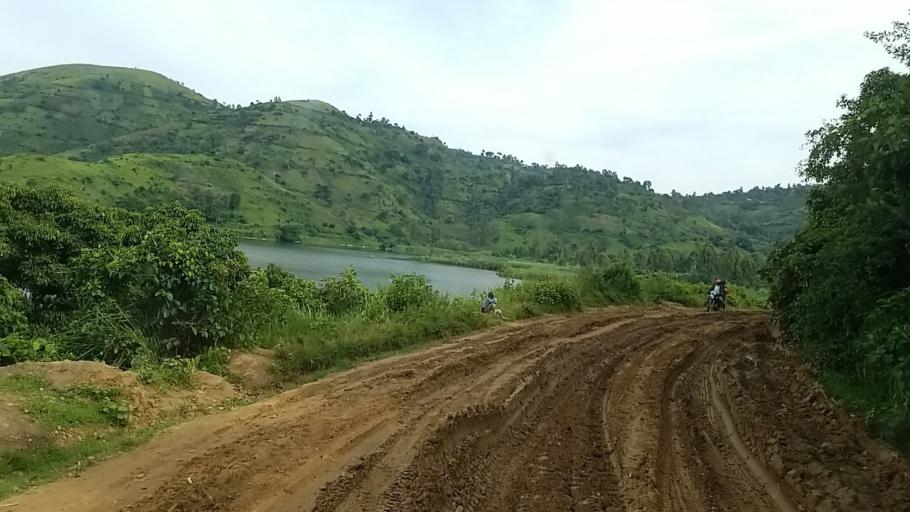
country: CD
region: Nord Kivu
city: Sake
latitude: -1.8000
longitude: 29.0115
